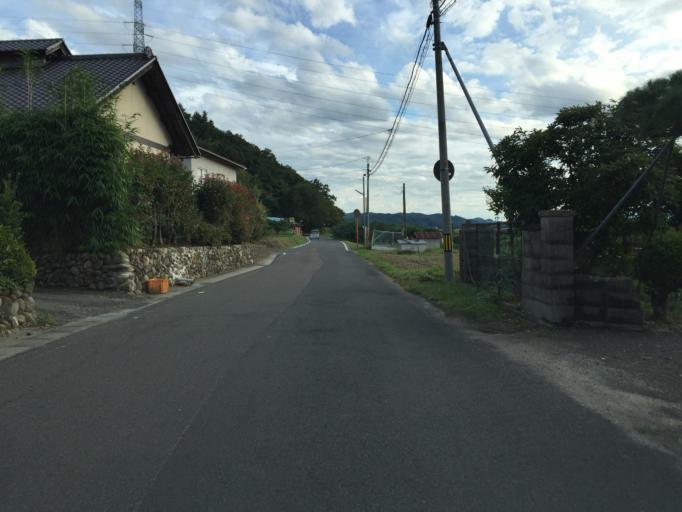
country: JP
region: Fukushima
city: Hobaramachi
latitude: 37.8043
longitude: 140.5097
